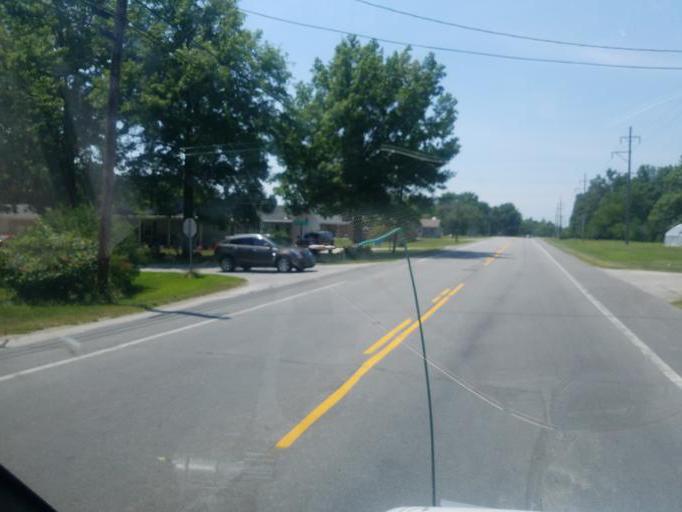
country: US
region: Ohio
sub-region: Auglaize County
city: Saint Marys
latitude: 40.5468
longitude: -84.4283
